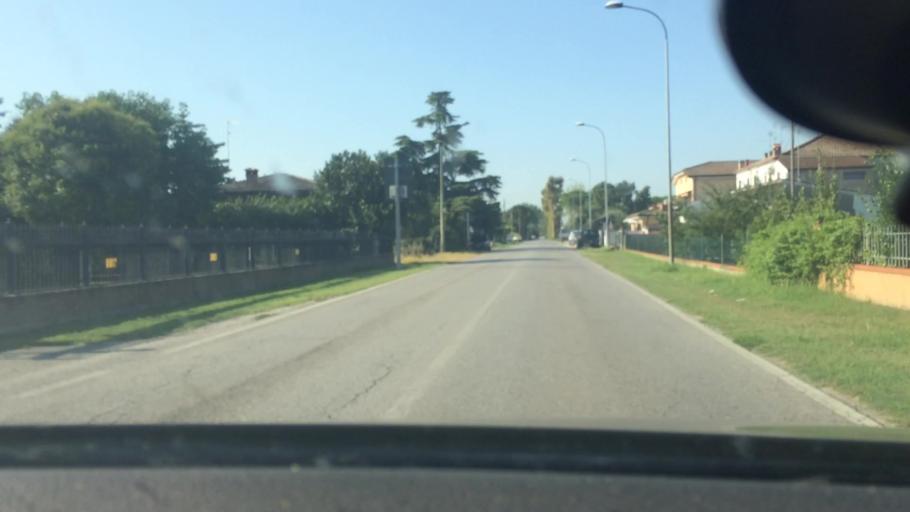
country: IT
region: Emilia-Romagna
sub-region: Provincia di Ferrara
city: Lagosanto
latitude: 44.7545
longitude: 12.1380
